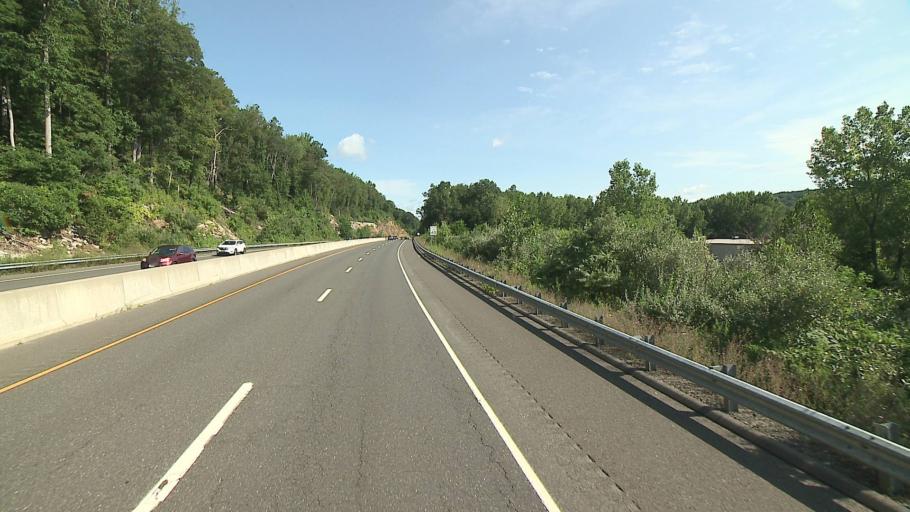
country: US
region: Connecticut
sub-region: Litchfield County
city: New Milford
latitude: 41.4917
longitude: -73.4196
